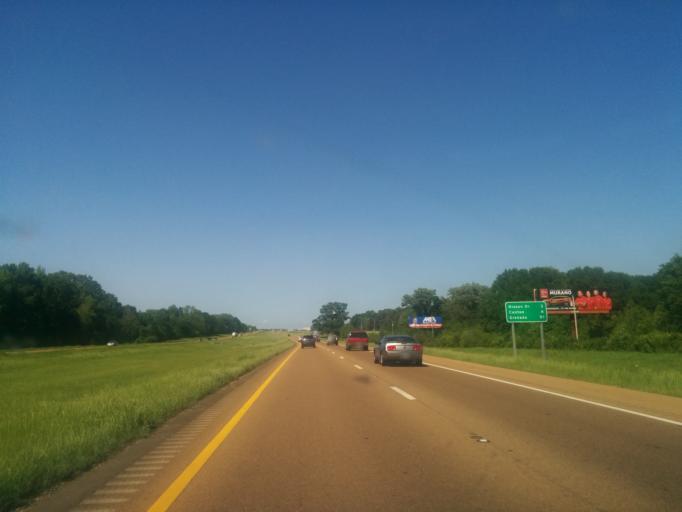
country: US
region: Mississippi
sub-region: Madison County
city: Canton
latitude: 32.5523
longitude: -90.0873
